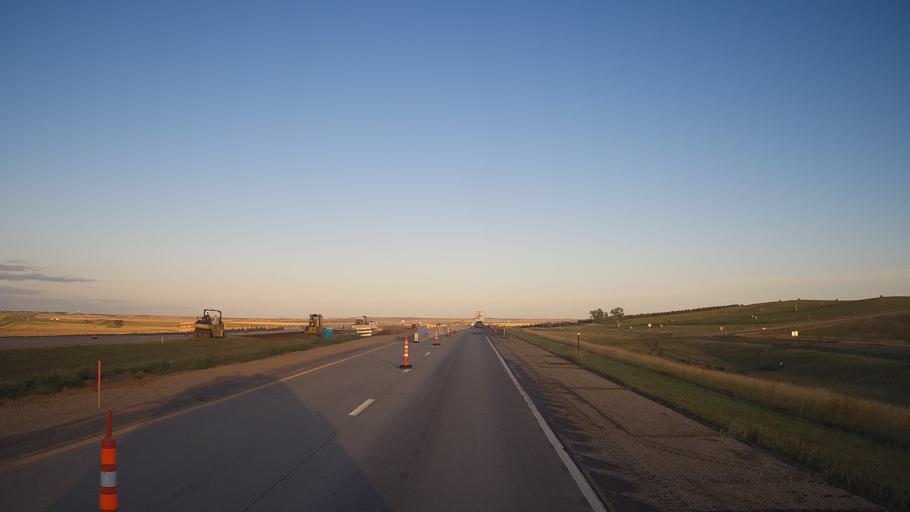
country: US
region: South Dakota
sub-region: Lyman County
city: Kennebec
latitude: 43.9047
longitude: -100.1685
